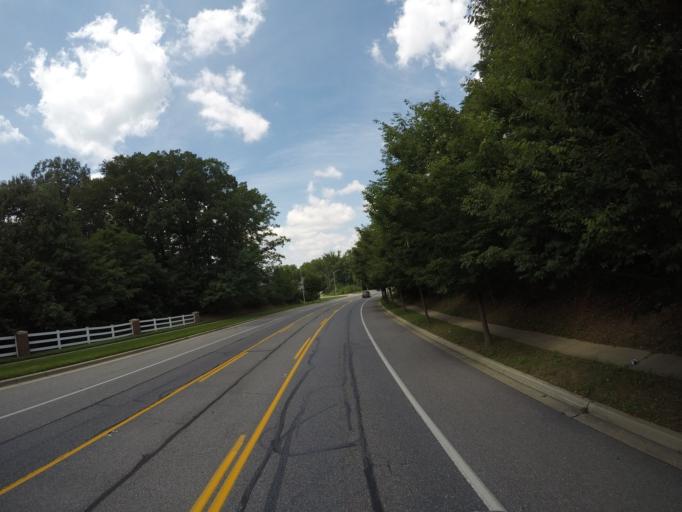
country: US
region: Maryland
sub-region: Anne Arundel County
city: Odenton
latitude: 39.0650
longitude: -76.7045
